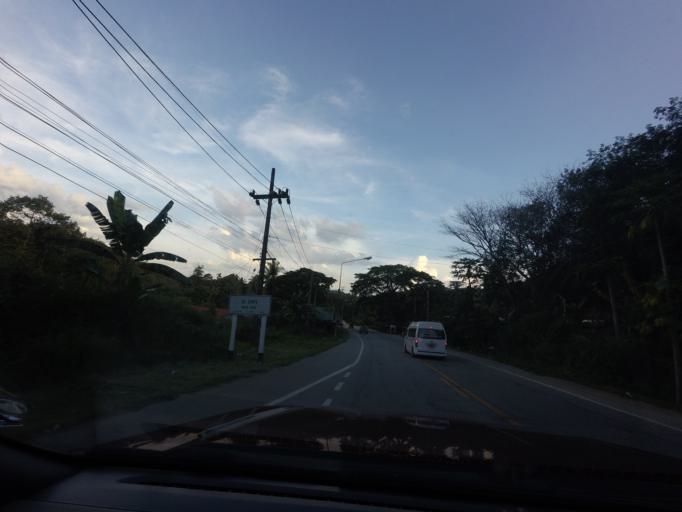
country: TH
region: Yala
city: Than To
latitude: 6.1297
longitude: 101.1918
